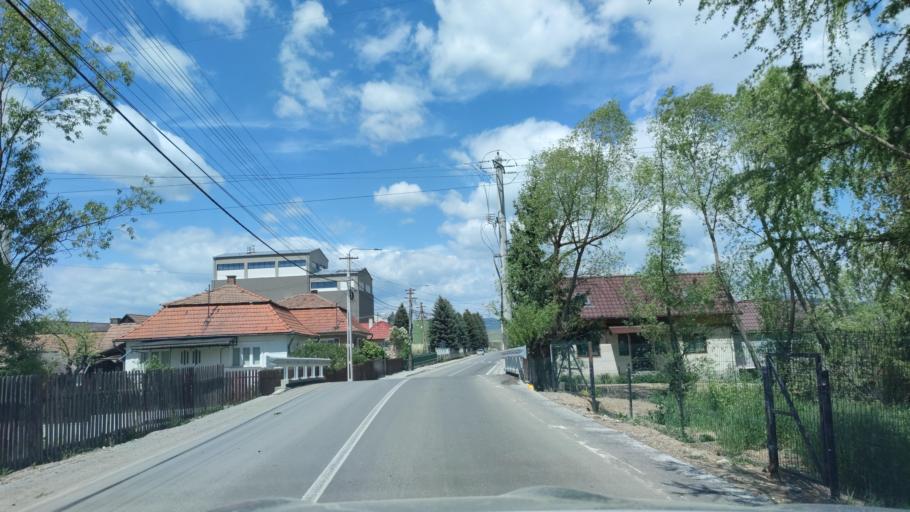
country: RO
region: Harghita
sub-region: Comuna Remetea
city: Remetea
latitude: 46.8111
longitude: 25.4592
